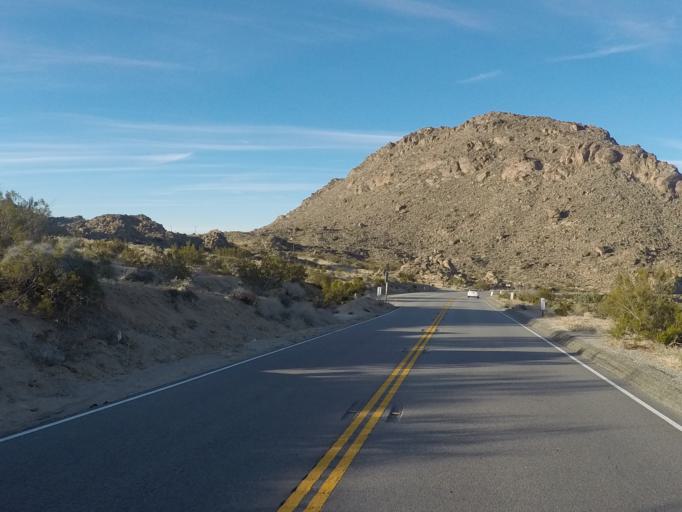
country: US
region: California
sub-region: Riverside County
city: Palm Desert
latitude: 33.6201
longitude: -116.4119
